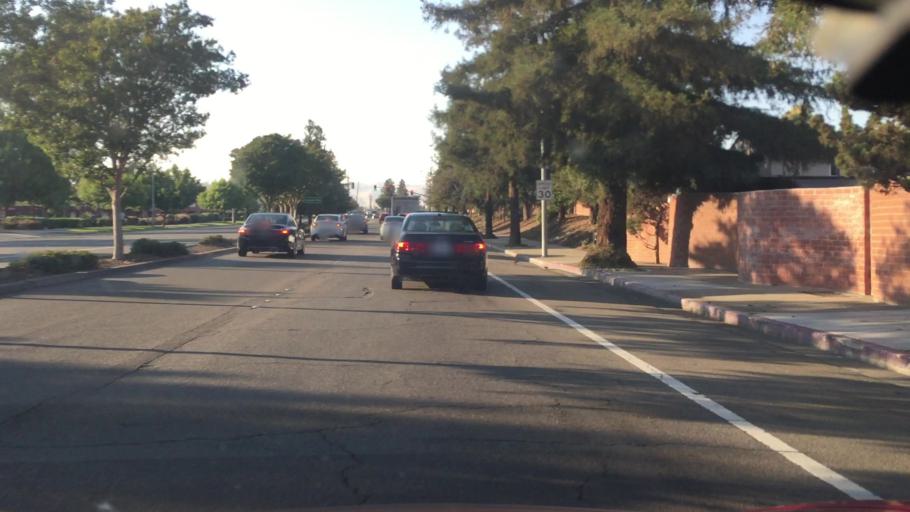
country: US
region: California
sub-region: Alameda County
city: Livermore
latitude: 37.6916
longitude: -121.7730
